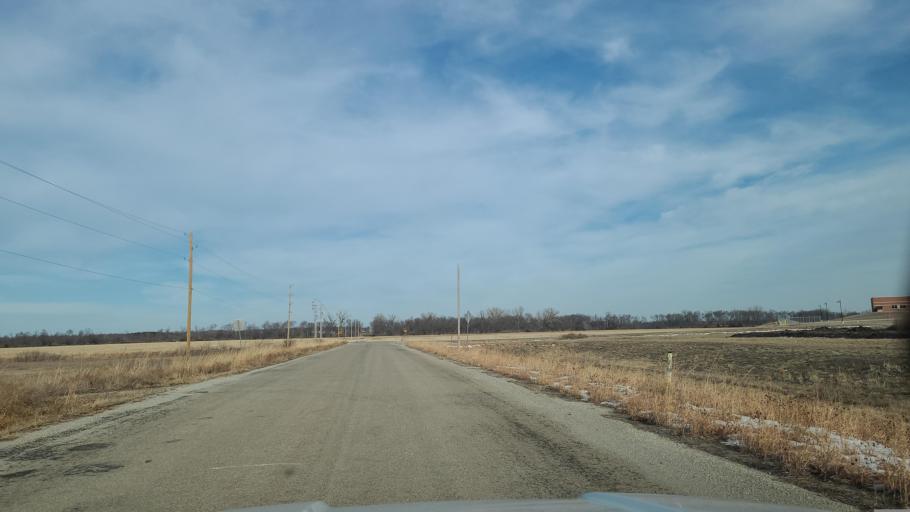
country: US
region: Kansas
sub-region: Douglas County
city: Lawrence
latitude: 38.9083
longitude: -95.2052
